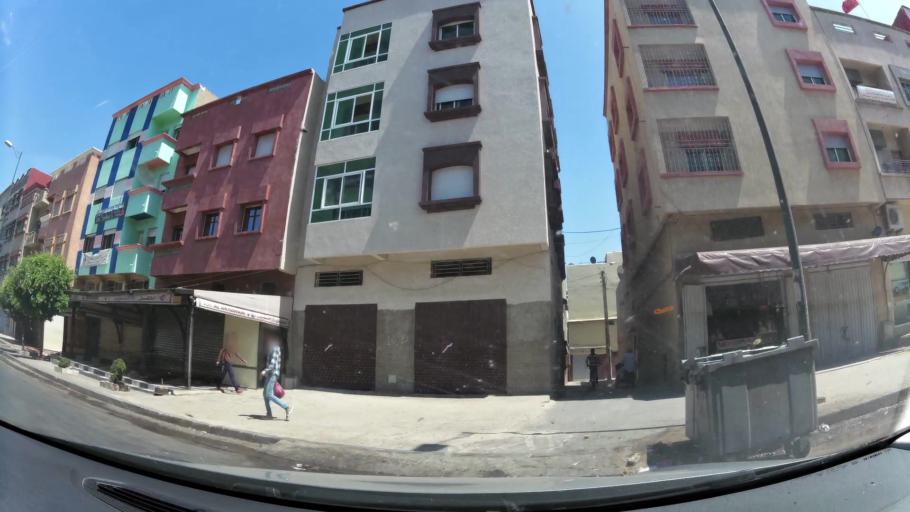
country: MA
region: Gharb-Chrarda-Beni Hssen
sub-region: Kenitra Province
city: Kenitra
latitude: 34.2474
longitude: -6.5446
